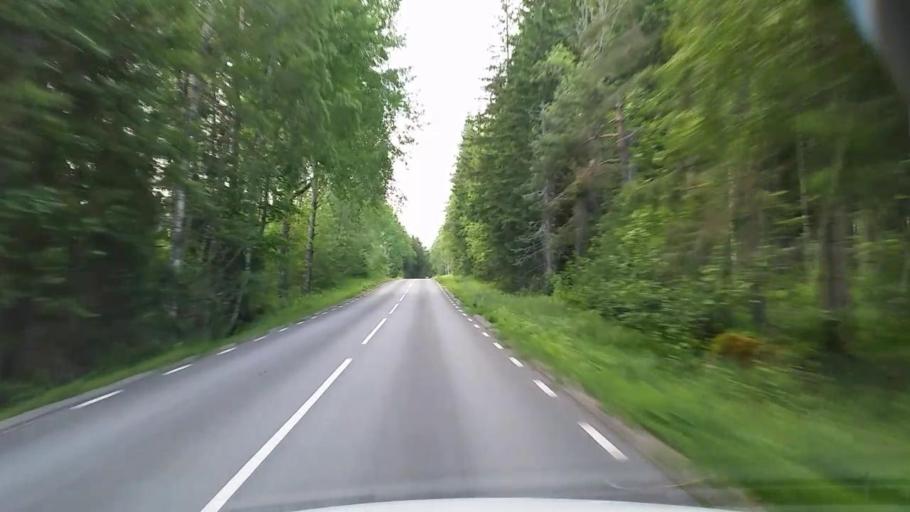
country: SE
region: Vaestmanland
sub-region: Kopings Kommun
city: Kolsva
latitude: 59.7526
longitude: 15.8321
